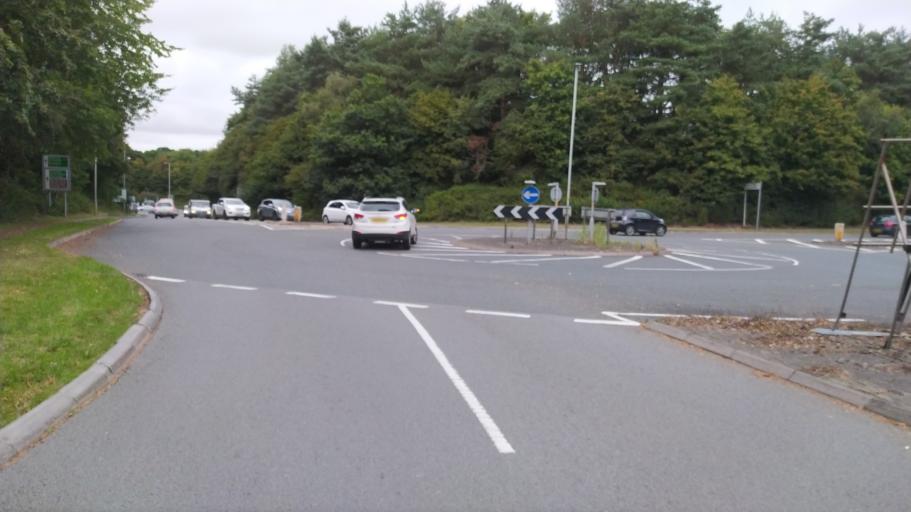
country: GB
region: England
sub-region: Dorset
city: Wimborne Minster
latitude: 50.7852
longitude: -1.9778
